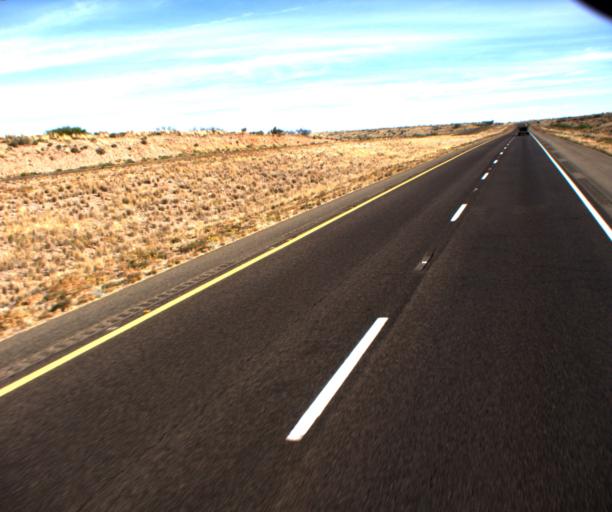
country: US
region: Arizona
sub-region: Cochise County
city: Willcox
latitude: 32.3866
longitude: -109.6659
